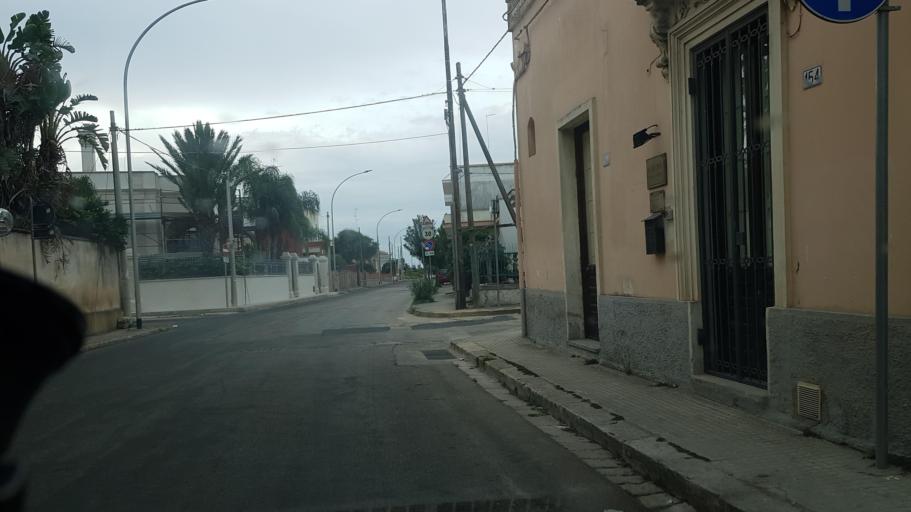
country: IT
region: Apulia
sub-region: Provincia di Lecce
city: Leverano
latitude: 40.2858
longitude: 18.0010
